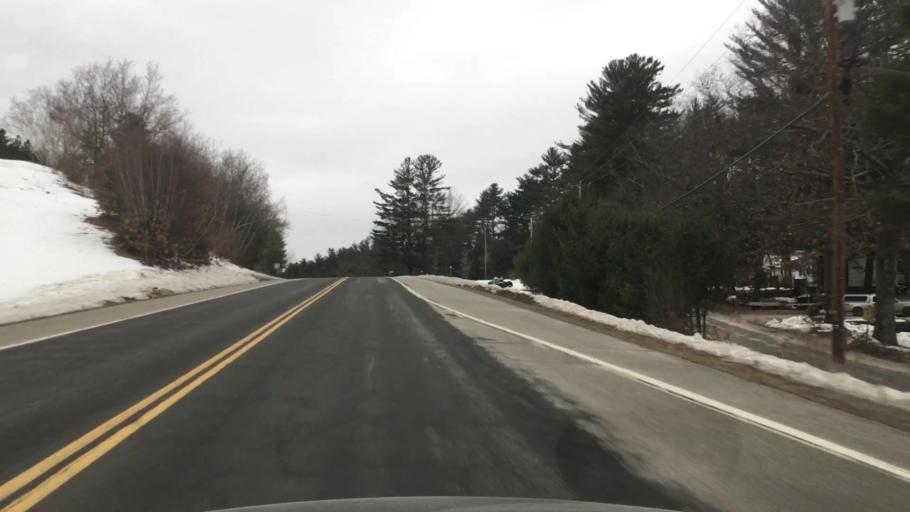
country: US
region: New Hampshire
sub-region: Merrimack County
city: Sutton
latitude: 43.2503
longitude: -71.9253
